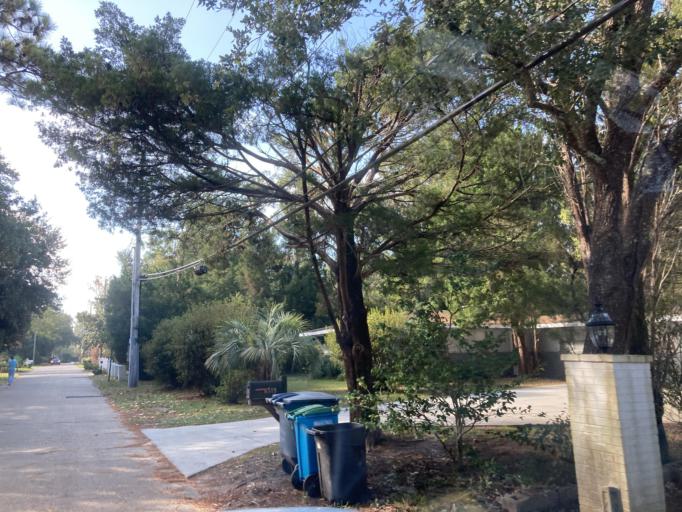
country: US
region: Mississippi
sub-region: Jackson County
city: Ocean Springs
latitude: 30.4121
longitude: -88.8333
